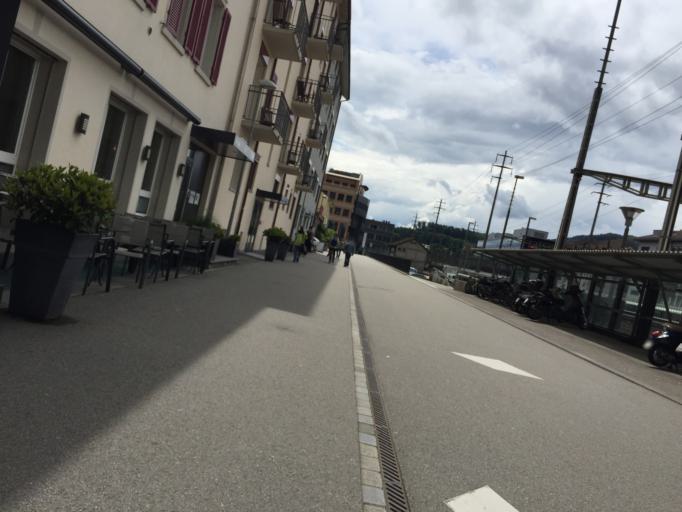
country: CH
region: Solothurn
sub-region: Bezirk Olten
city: Olten
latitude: 47.3508
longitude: 7.9082
